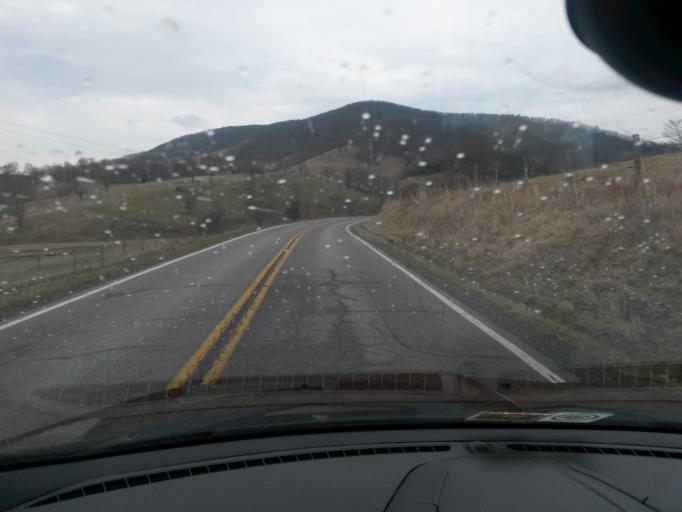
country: US
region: Virginia
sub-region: Highland County
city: Monterey
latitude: 38.3785
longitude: -79.6531
